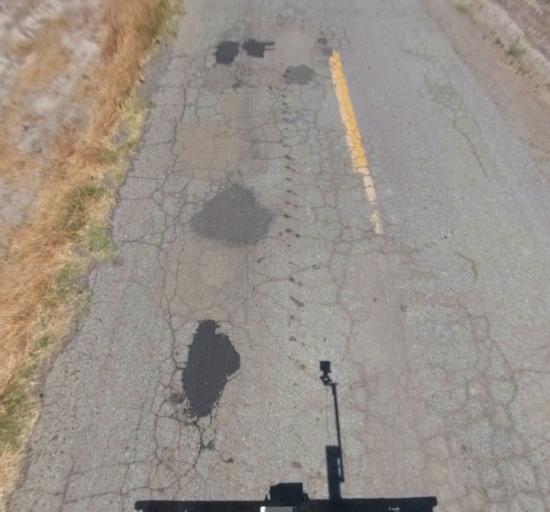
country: US
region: California
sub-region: Madera County
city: Chowchilla
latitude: 37.0110
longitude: -120.3077
